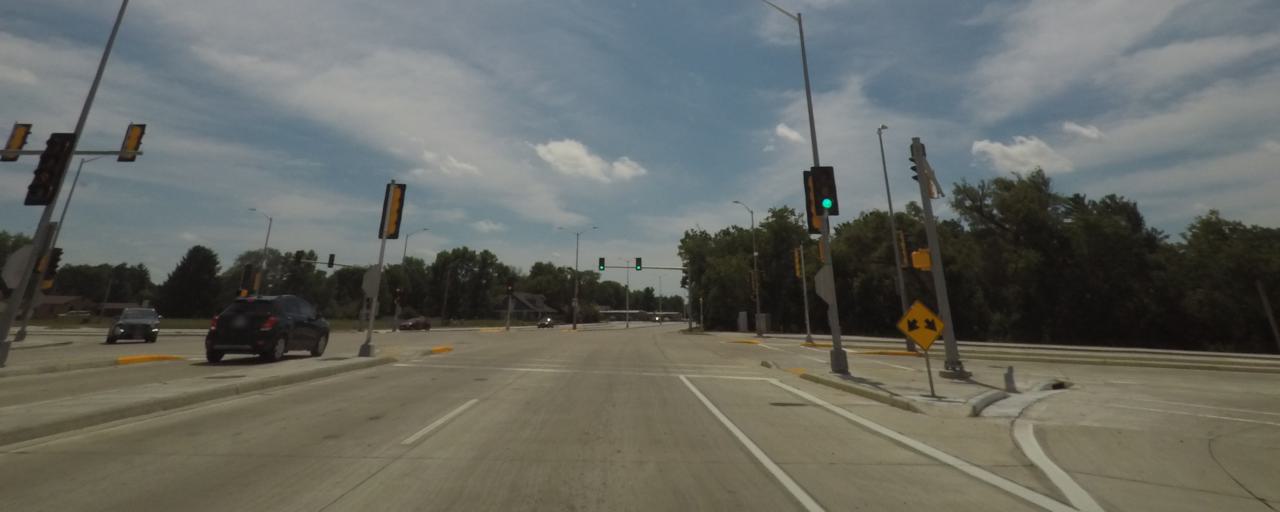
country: US
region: Wisconsin
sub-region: Portage County
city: Whiting
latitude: 44.4929
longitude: -89.5531
